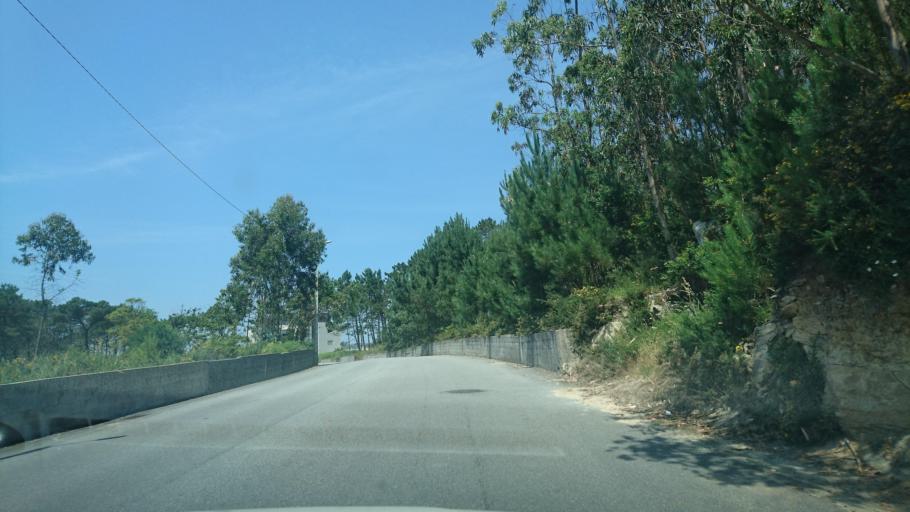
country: PT
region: Porto
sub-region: Matosinhos
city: Lavra
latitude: 41.2712
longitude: -8.7216
